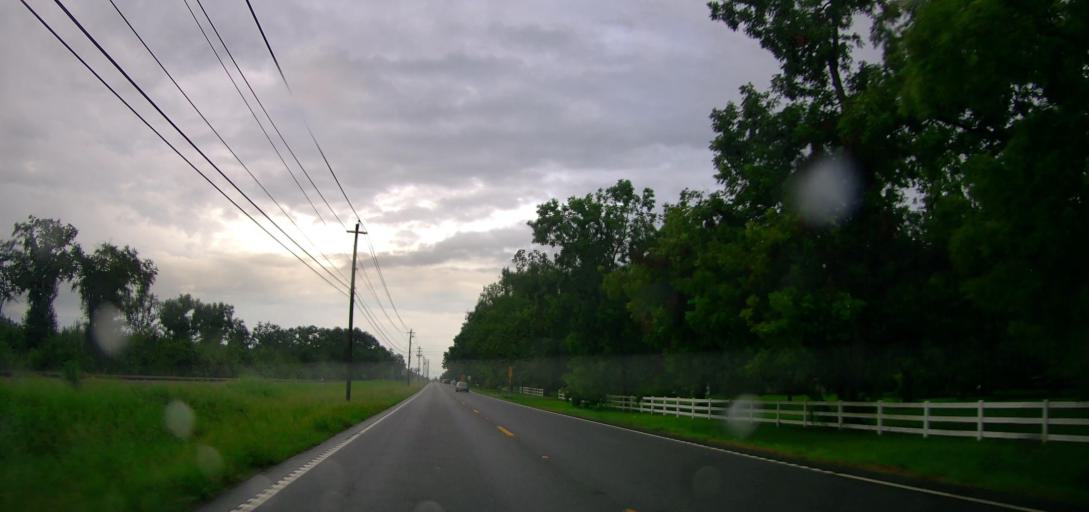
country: US
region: Georgia
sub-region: Ware County
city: Deenwood
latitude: 31.2443
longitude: -82.3734
